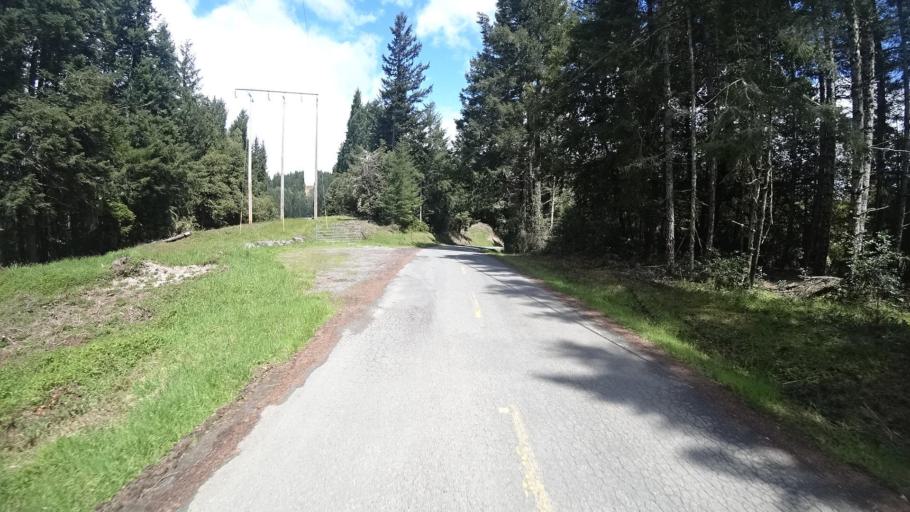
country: US
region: California
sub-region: Humboldt County
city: Blue Lake
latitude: 40.7613
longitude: -123.9611
